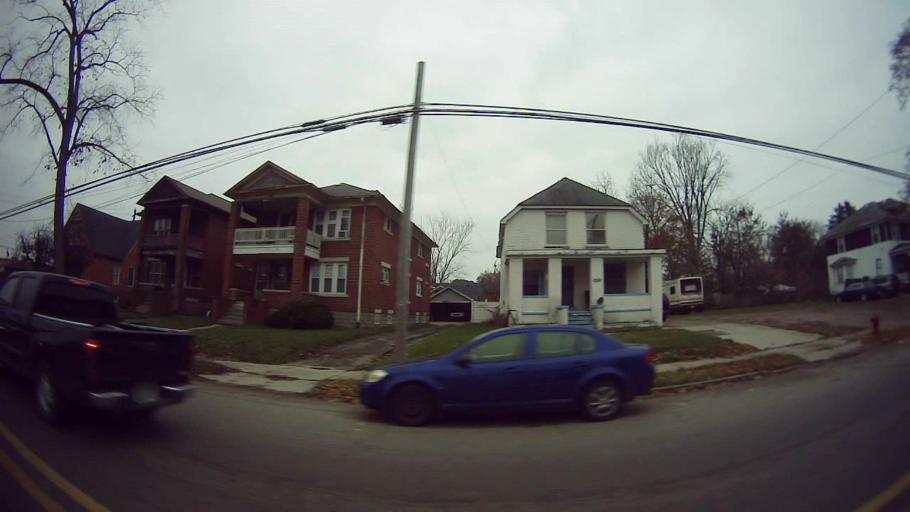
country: US
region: Michigan
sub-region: Wayne County
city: Redford
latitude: 42.4194
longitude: -83.2579
